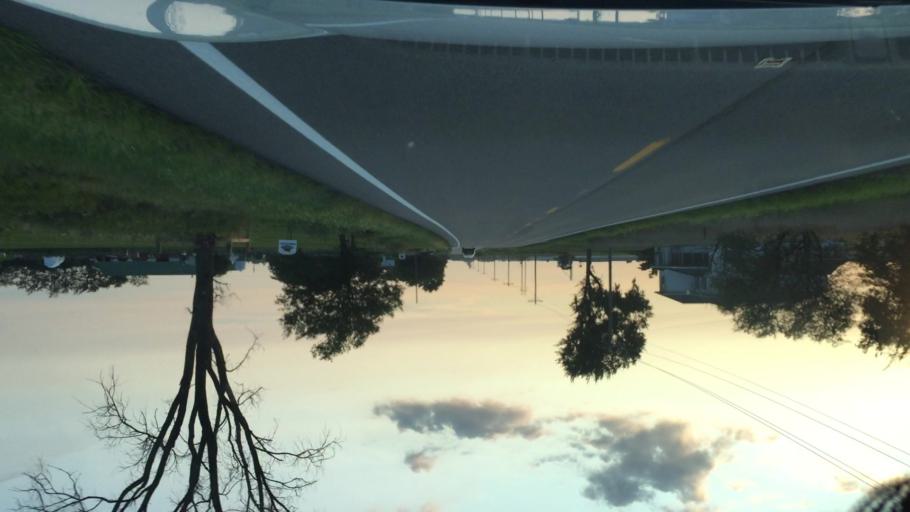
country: US
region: Ohio
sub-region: Champaign County
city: Mechanicsburg
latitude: 40.0518
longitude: -83.5256
